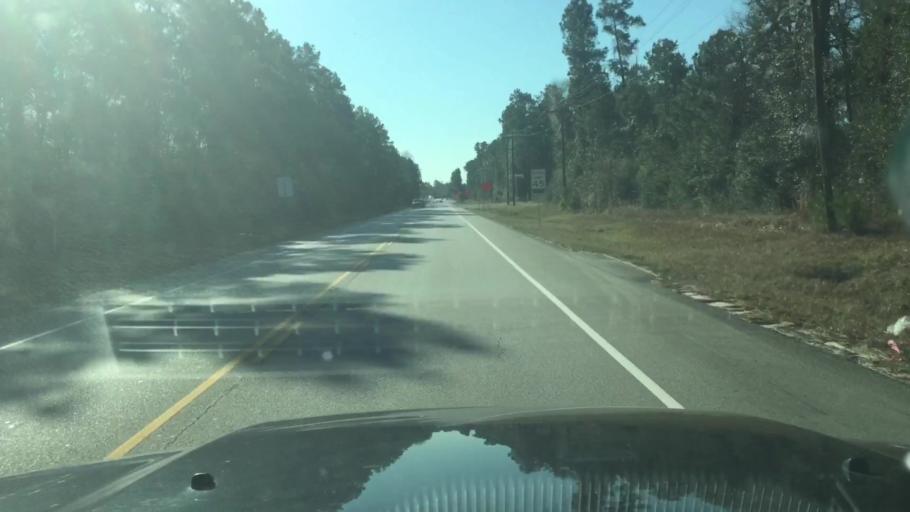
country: US
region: Texas
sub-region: Montgomery County
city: Porter Heights
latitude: 30.2218
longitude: -95.3603
